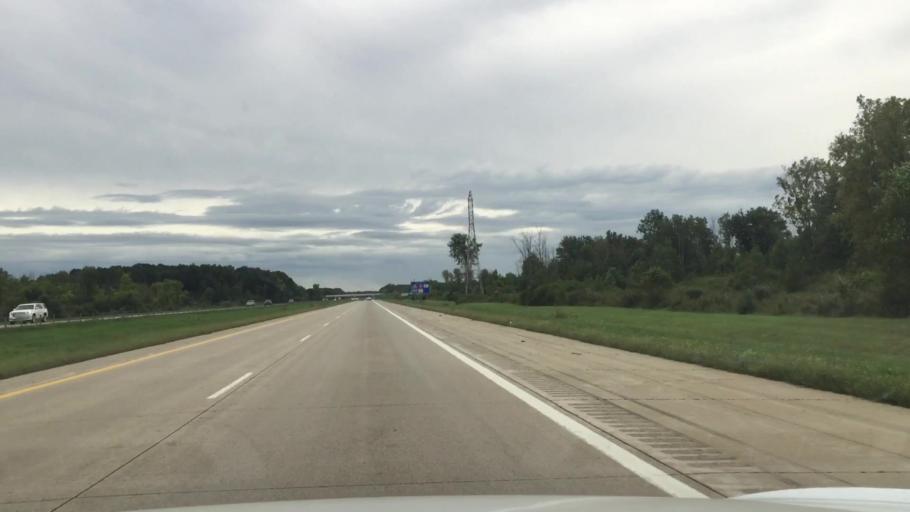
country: US
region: Michigan
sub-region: Saint Clair County
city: Marysville
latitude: 42.9301
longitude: -82.5068
